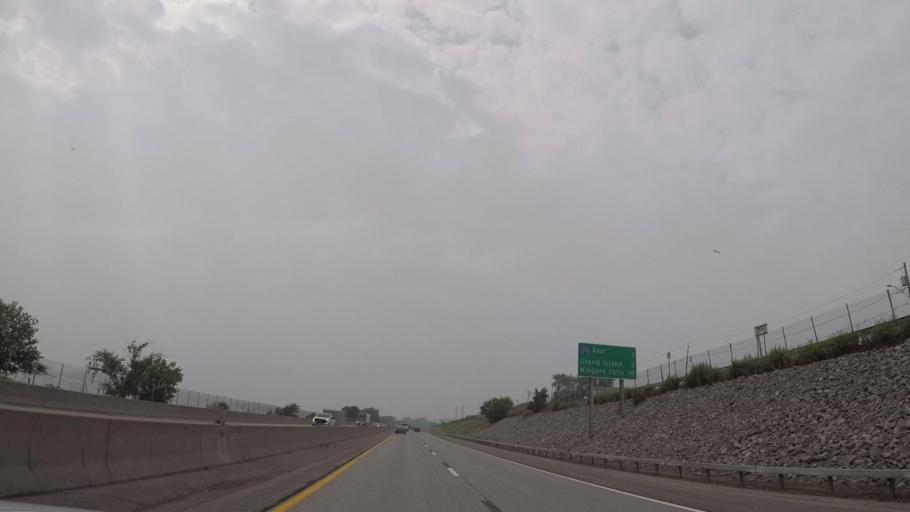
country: US
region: New York
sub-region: Erie County
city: Kenmore
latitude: 42.9568
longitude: -78.9128
